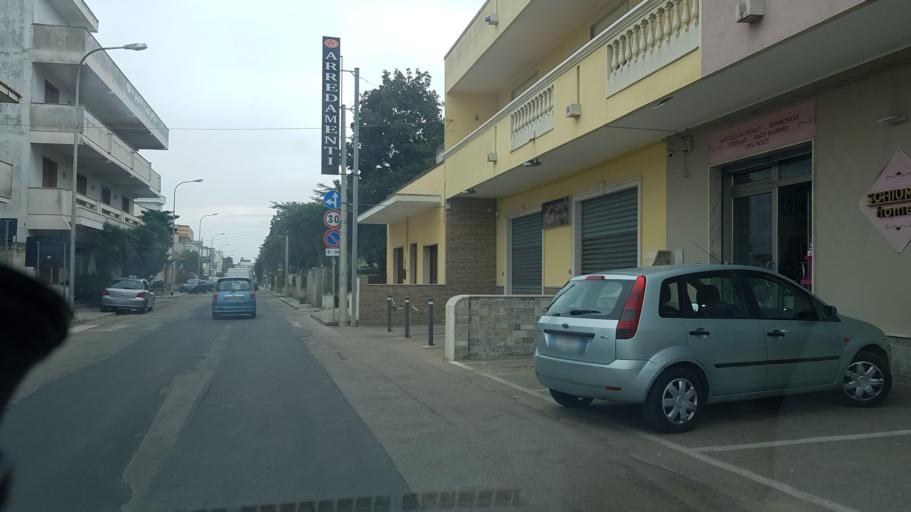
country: IT
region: Apulia
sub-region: Provincia di Lecce
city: Leverano
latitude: 40.2973
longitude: 17.9948
